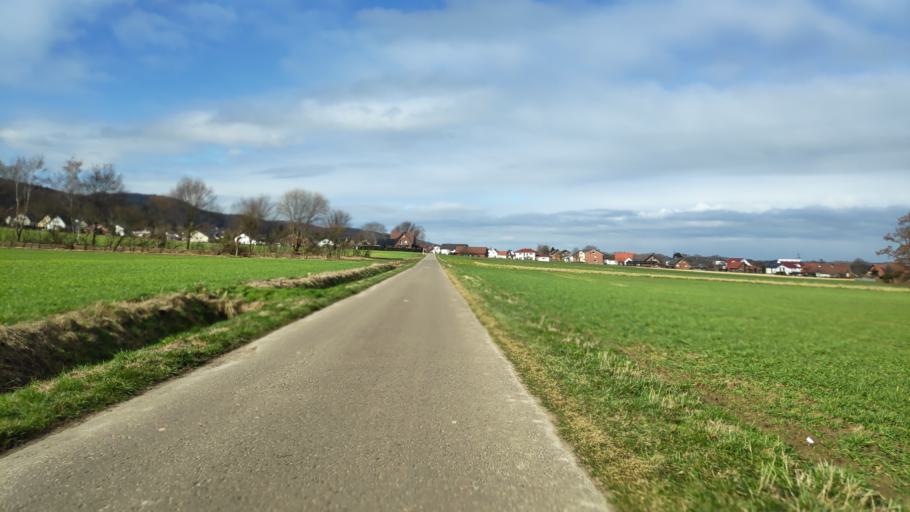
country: DE
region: North Rhine-Westphalia
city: Bad Oeynhausen
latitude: 52.2709
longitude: 8.8020
